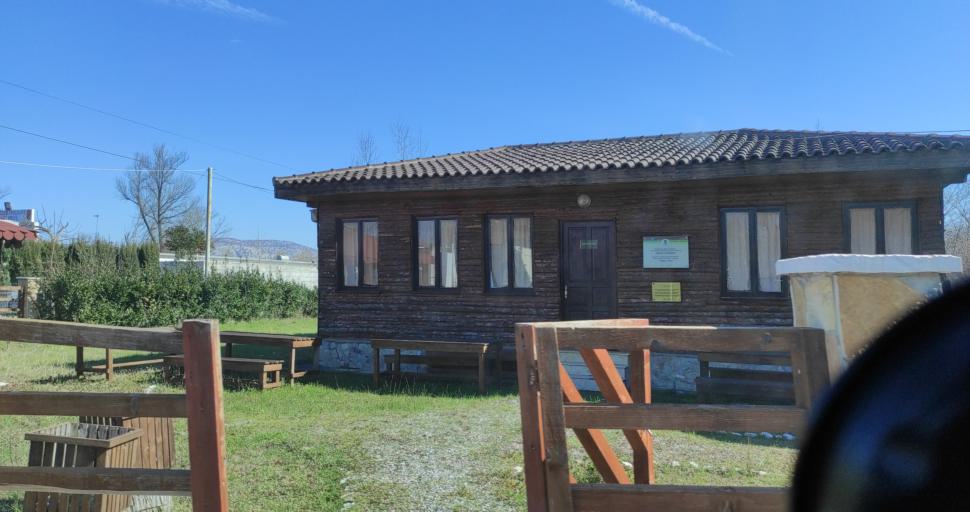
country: AL
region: Shkoder
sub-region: Rrethi i Shkodres
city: Velipoje
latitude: 41.8660
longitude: 19.4062
